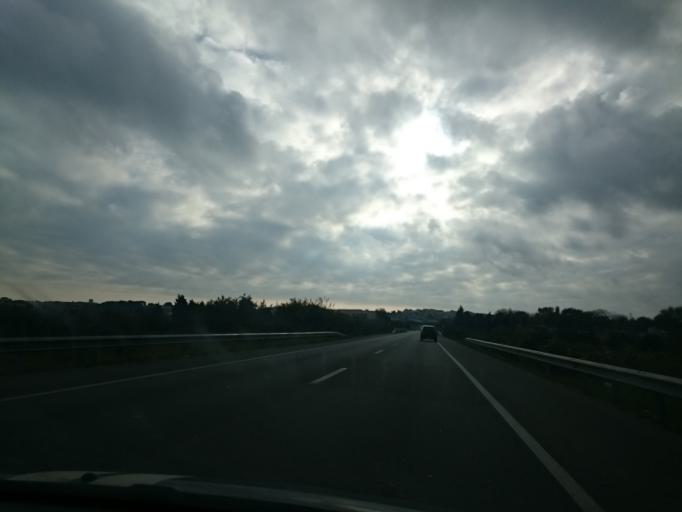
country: ES
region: Catalonia
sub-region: Provincia de Barcelona
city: Vilanova i la Geltru
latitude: 41.2309
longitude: 1.7090
